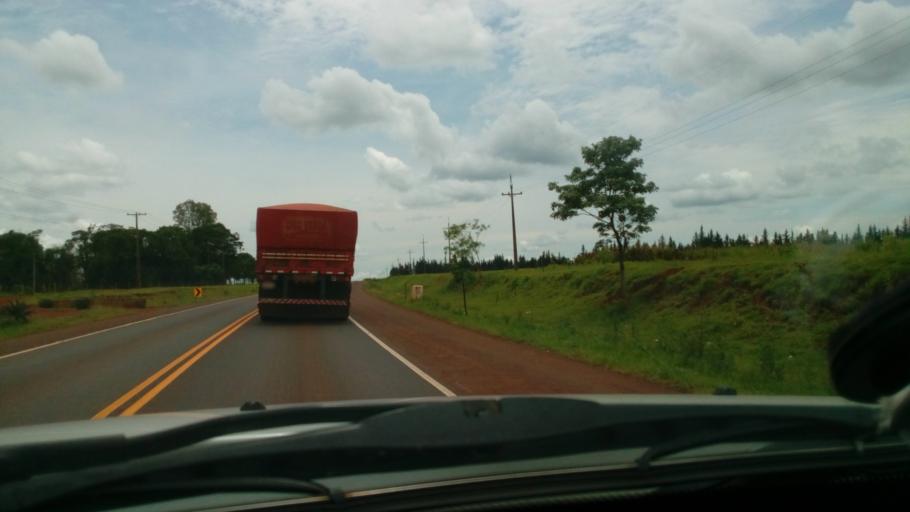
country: PY
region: Alto Parana
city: Colonia Yguazu
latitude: -25.5860
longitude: -54.9288
